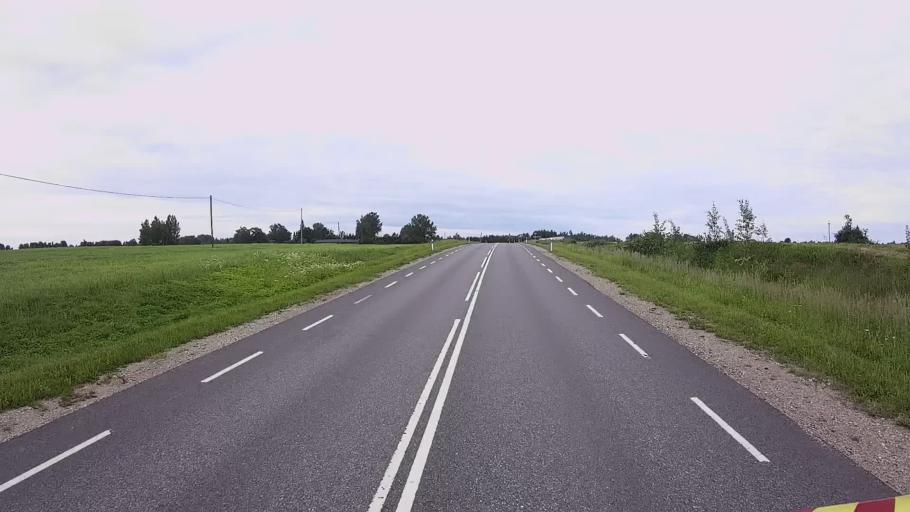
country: EE
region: Viljandimaa
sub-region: Karksi vald
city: Karksi-Nuia
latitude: 58.1454
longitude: 25.5909
